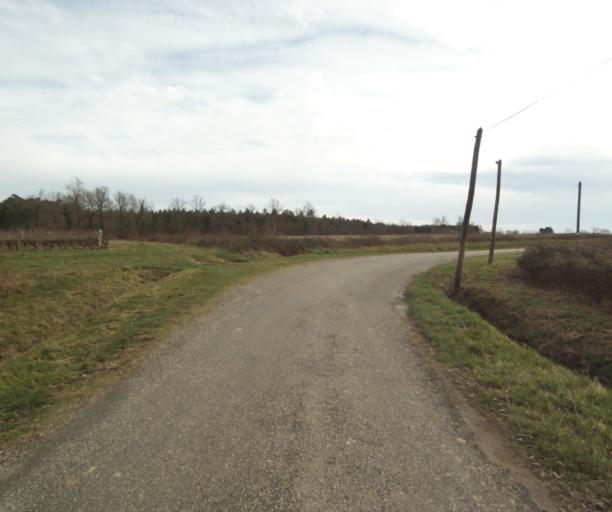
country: FR
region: Aquitaine
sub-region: Departement des Landes
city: Gabarret
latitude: 43.9659
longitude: 0.0387
